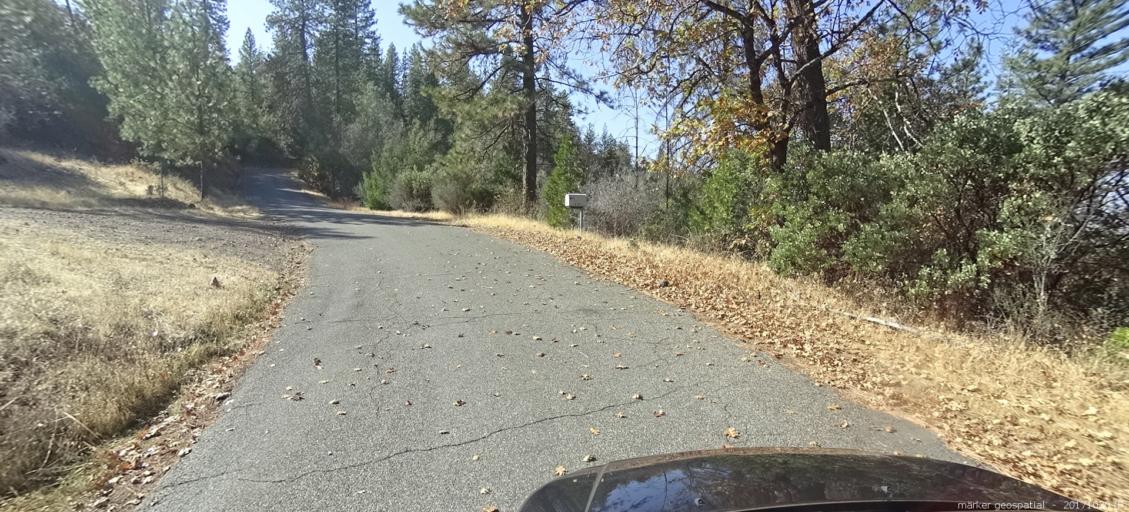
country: US
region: California
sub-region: Shasta County
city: Shingletown
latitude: 40.5862
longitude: -121.8653
